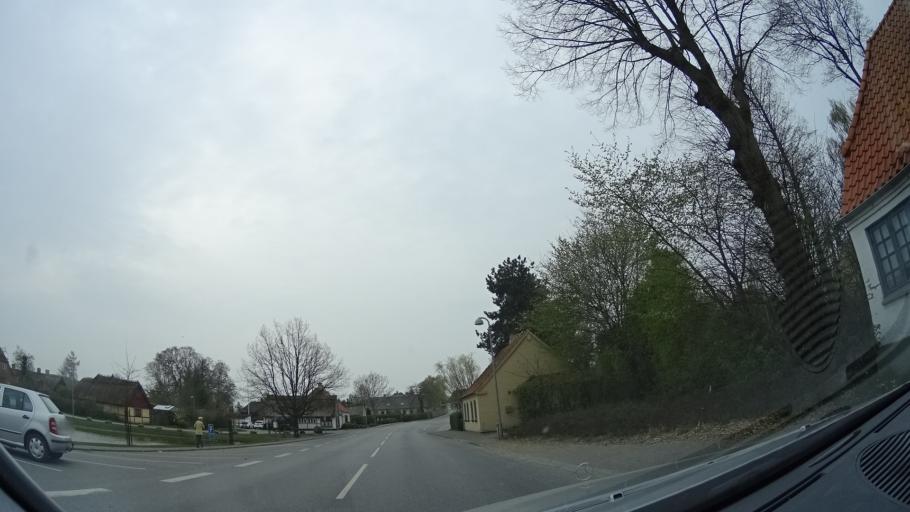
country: DK
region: Zealand
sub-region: Lejre Kommune
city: Ejby
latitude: 55.7077
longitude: 11.9004
